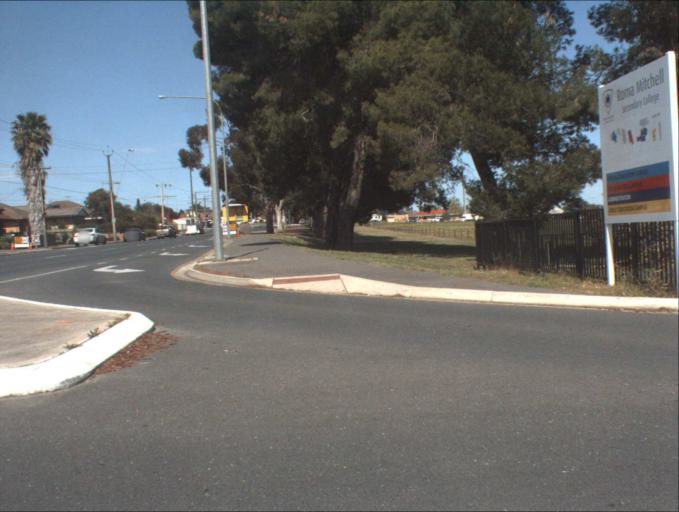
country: AU
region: South Australia
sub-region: Port Adelaide Enfield
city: Enfield
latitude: -34.8453
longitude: 138.6185
